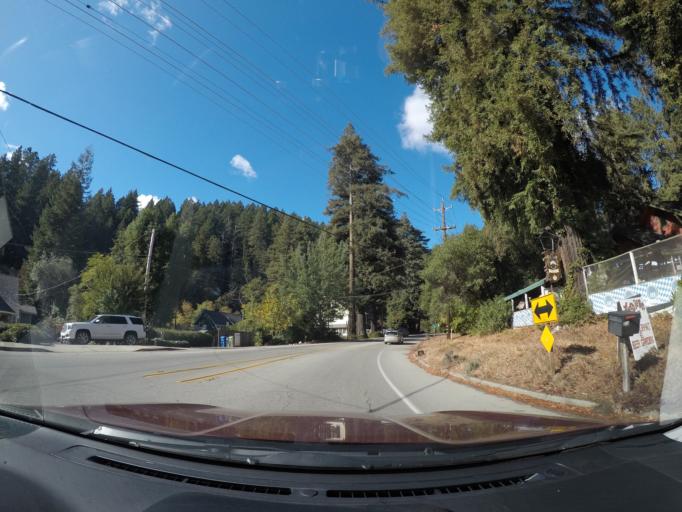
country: US
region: California
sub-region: Santa Cruz County
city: Ben Lomond
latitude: 37.0894
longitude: -122.0922
